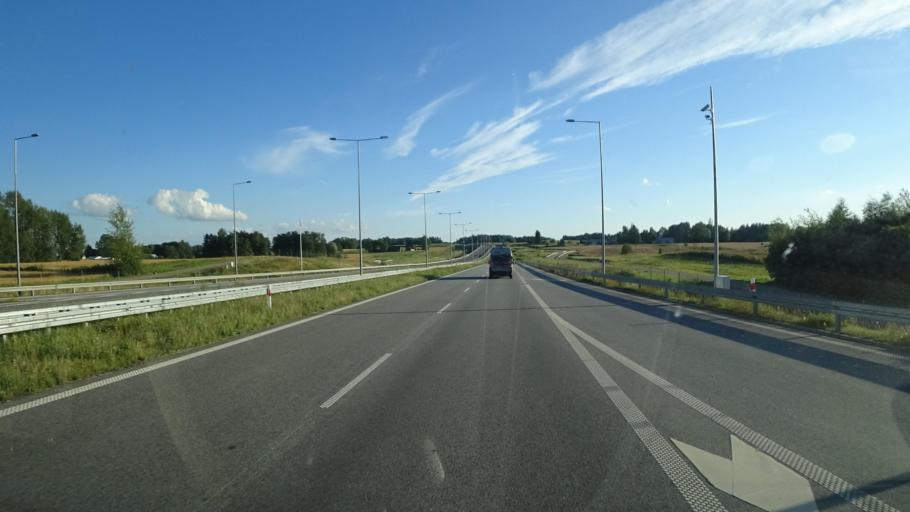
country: PL
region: Podlasie
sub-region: Powiat suwalski
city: Raczki
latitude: 53.9679
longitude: 22.7817
